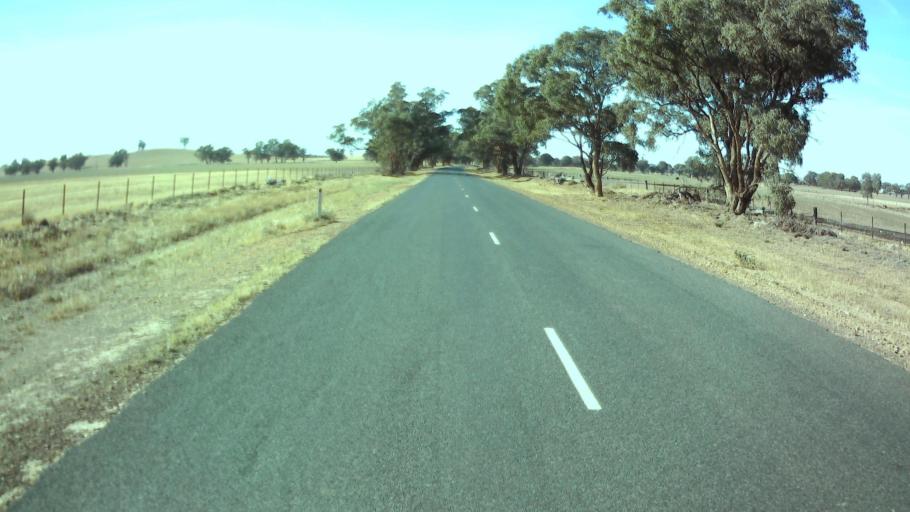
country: AU
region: New South Wales
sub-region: Weddin
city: Grenfell
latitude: -33.9550
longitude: 148.1391
